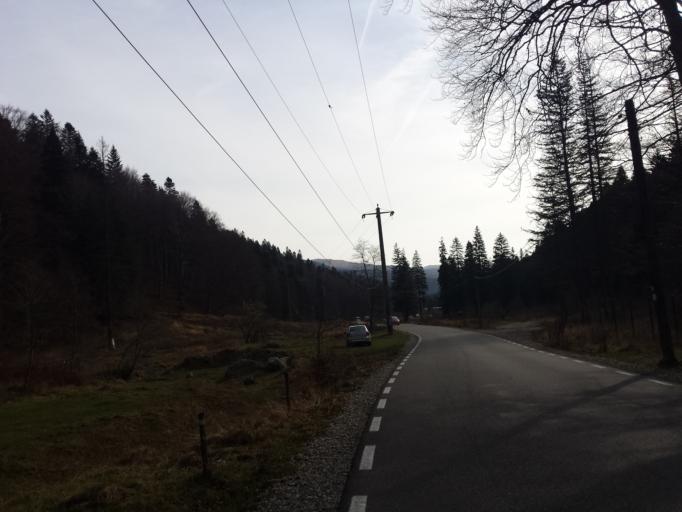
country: RO
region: Prahova
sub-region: Oras Azuga
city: Azuga
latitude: 45.4476
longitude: 25.5217
